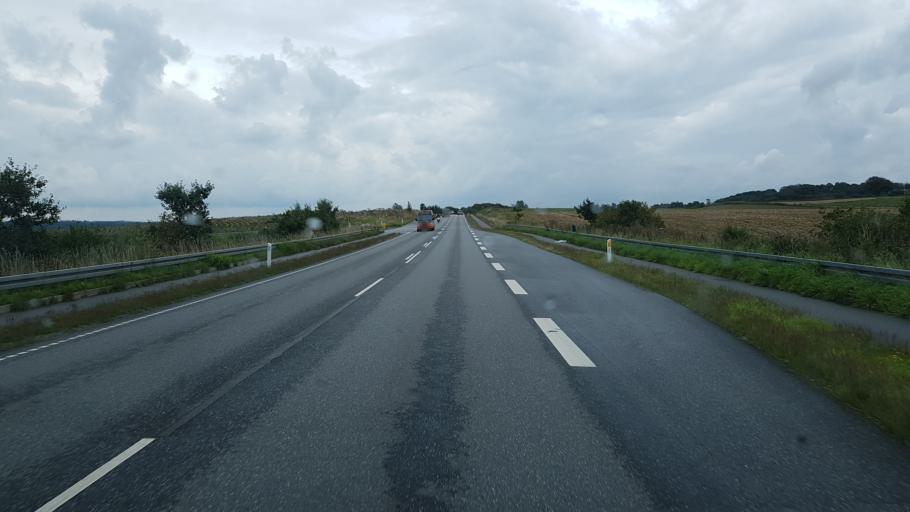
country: DK
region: Central Jutland
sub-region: Horsens Kommune
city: Horsens
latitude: 55.9052
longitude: 9.7379
